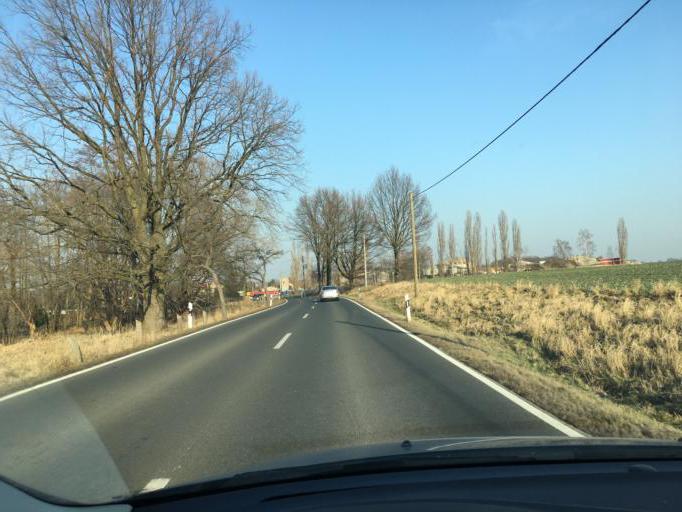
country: DE
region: Saxony
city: Bad Lausick
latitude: 51.1406
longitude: 12.6140
